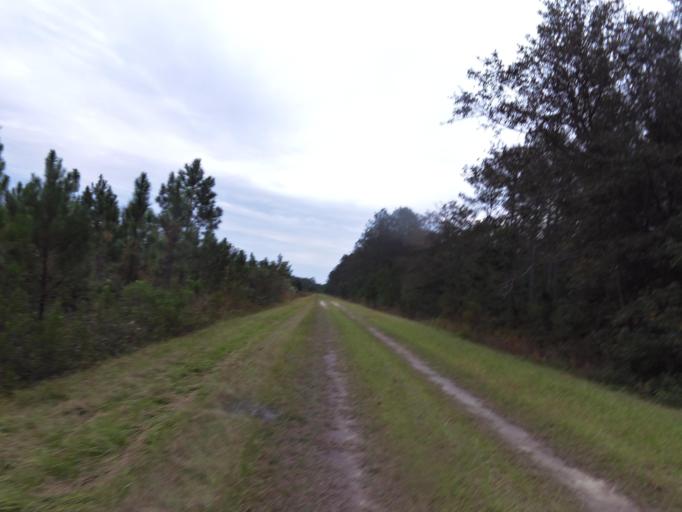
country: US
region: Florida
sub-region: Putnam County
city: Palatka
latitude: 29.6793
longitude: -81.7455
